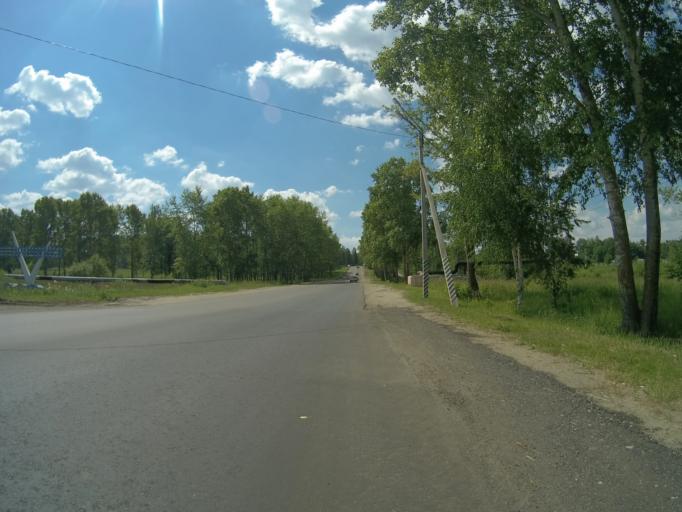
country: RU
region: Kostroma
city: Volgorechensk
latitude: 57.4442
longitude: 41.1630
